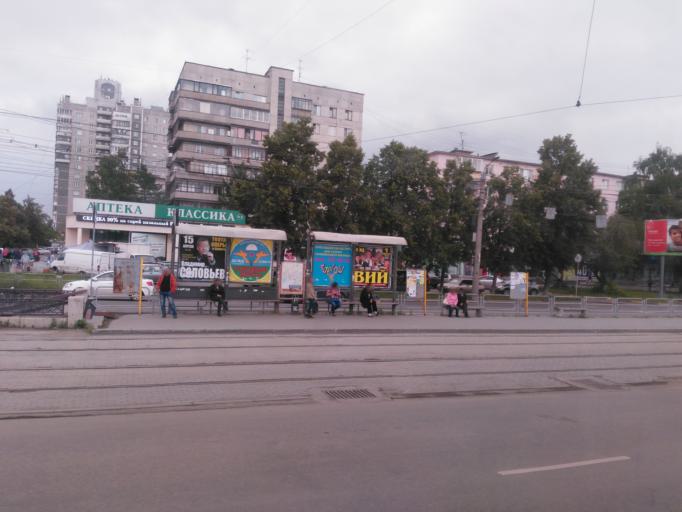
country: RU
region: Chelyabinsk
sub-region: Gorod Chelyabinsk
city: Chelyabinsk
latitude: 55.1839
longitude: 61.3987
